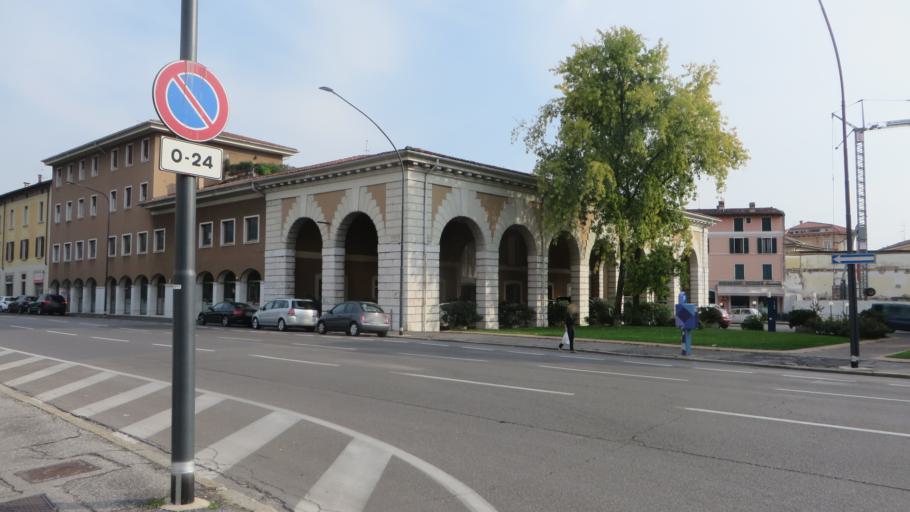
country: IT
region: Lombardy
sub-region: Provincia di Brescia
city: Brescia
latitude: 45.5327
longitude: 10.2231
